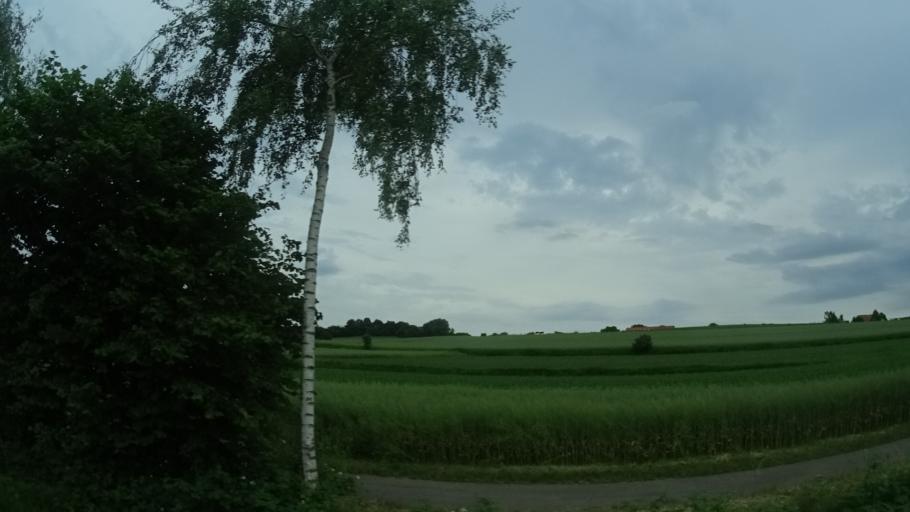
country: DE
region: North Rhine-Westphalia
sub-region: Regierungsbezirk Detmold
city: Schieder-Schwalenberg
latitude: 51.8467
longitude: 9.2825
